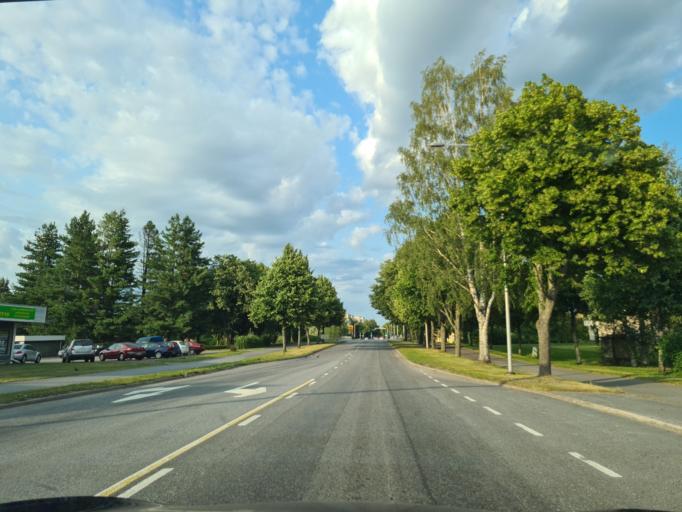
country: FI
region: Southern Ostrobothnia
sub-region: Seinaejoki
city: Lapua
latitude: 62.9704
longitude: 22.9973
